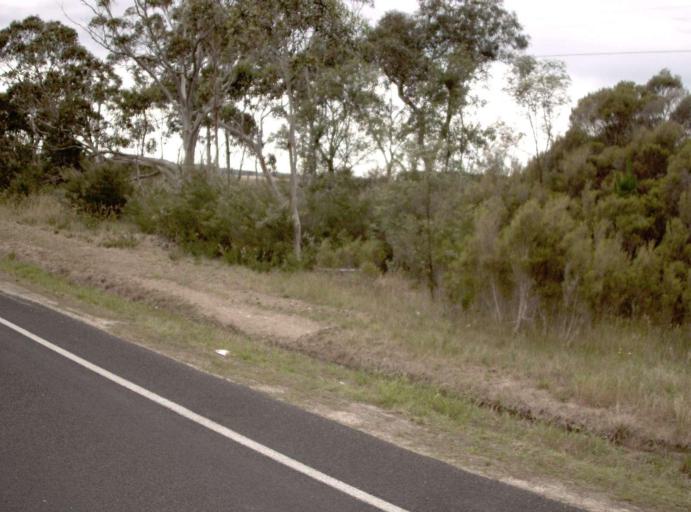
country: AU
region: Victoria
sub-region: Wellington
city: Sale
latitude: -38.2084
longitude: 147.0684
